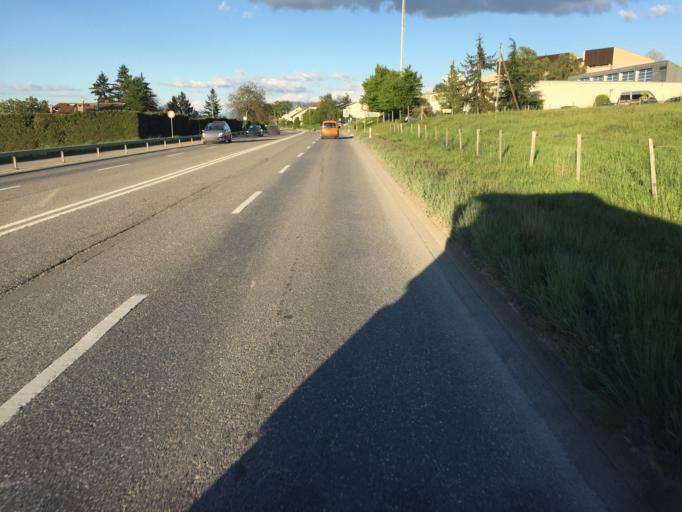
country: CH
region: Geneva
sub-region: Geneva
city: Bernex
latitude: 46.1751
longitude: 6.0618
